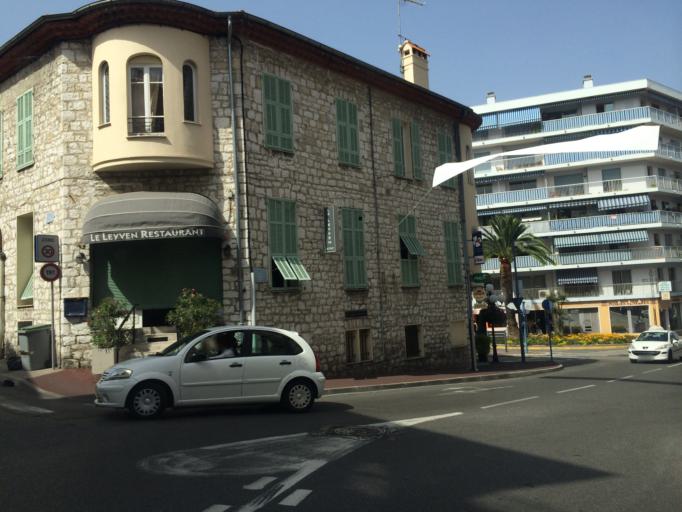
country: FR
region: Provence-Alpes-Cote d'Azur
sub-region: Departement des Alpes-Maritimes
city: Cagnes-sur-Mer
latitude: 43.6642
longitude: 7.1494
